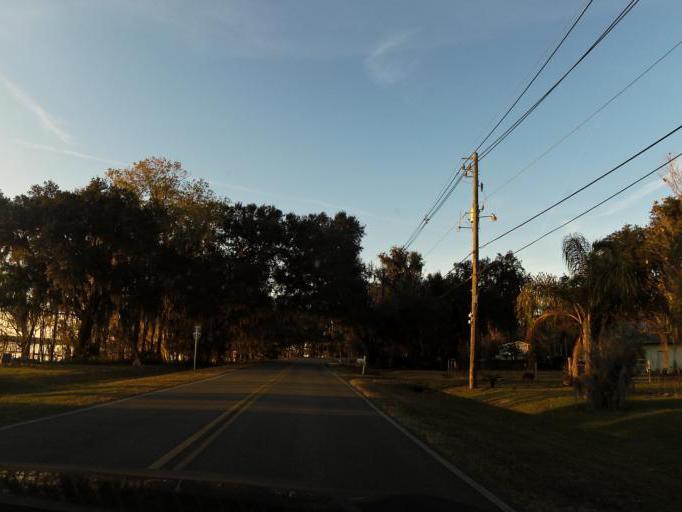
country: US
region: Florida
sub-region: Clay County
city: Green Cove Springs
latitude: 29.9155
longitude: -81.5935
